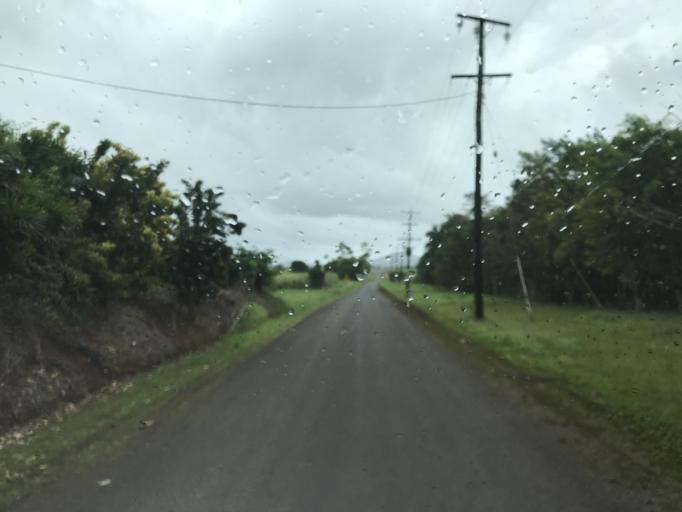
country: AU
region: Queensland
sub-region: Cassowary Coast
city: Innisfail
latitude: -17.4843
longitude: 145.9892
